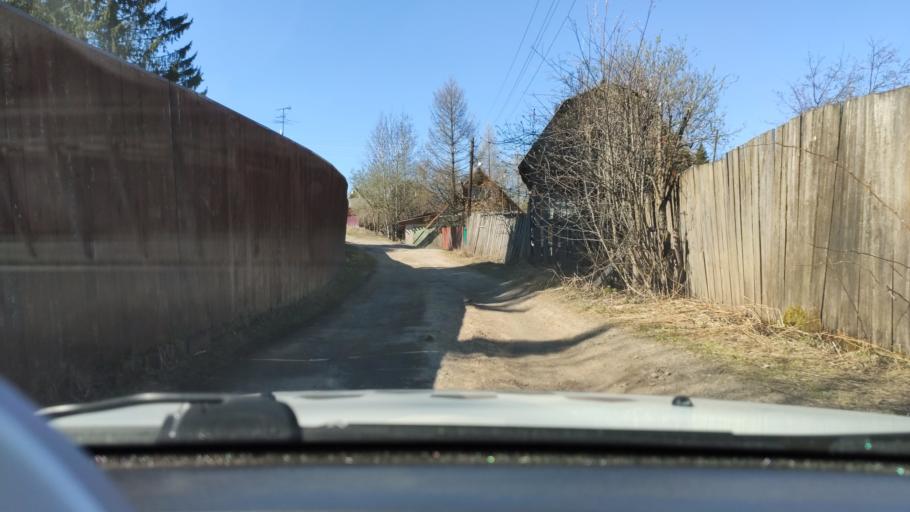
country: RU
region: Perm
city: Novyye Lyady
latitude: 58.0497
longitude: 56.6488
